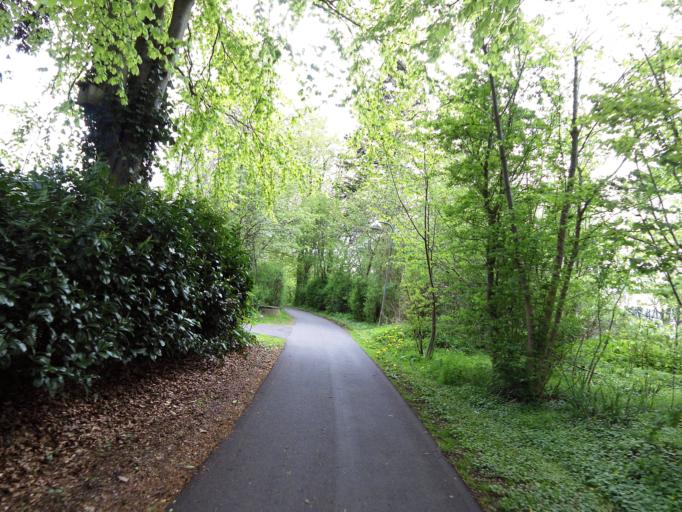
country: DK
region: South Denmark
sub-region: Haderslev Kommune
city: Gram
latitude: 55.2921
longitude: 9.0437
